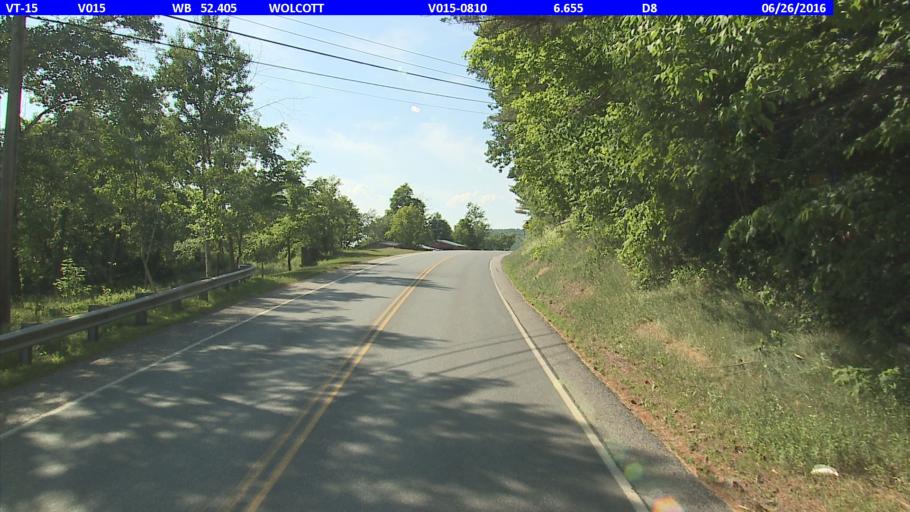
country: US
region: Vermont
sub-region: Caledonia County
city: Hardwick
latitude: 44.5293
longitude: -72.4232
